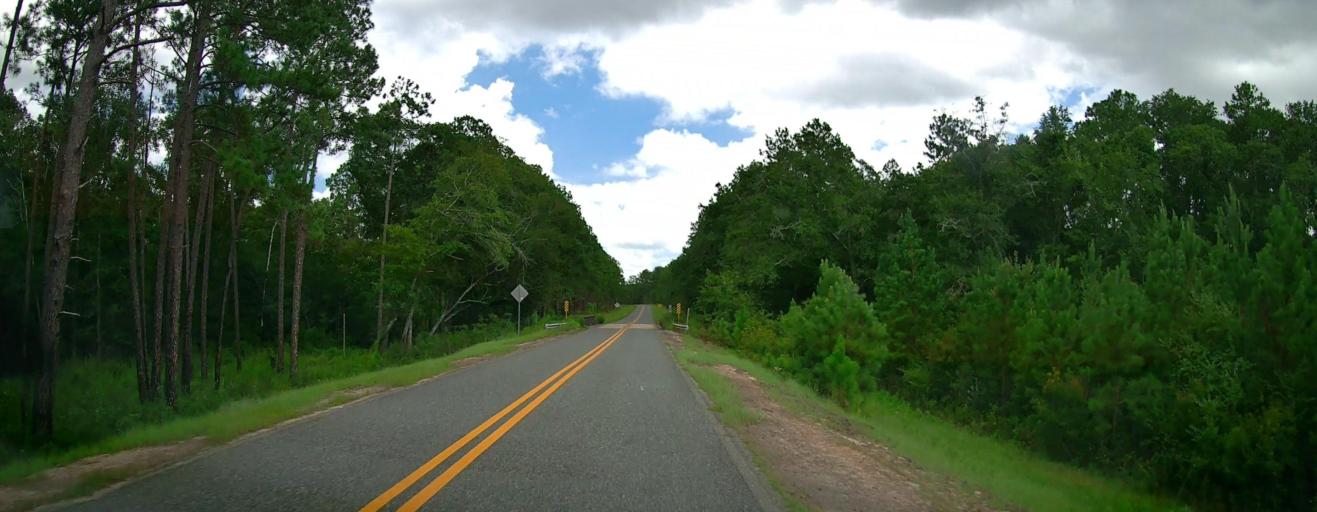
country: US
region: Georgia
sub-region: Turner County
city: Ashburn
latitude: 31.7030
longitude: -83.5032
